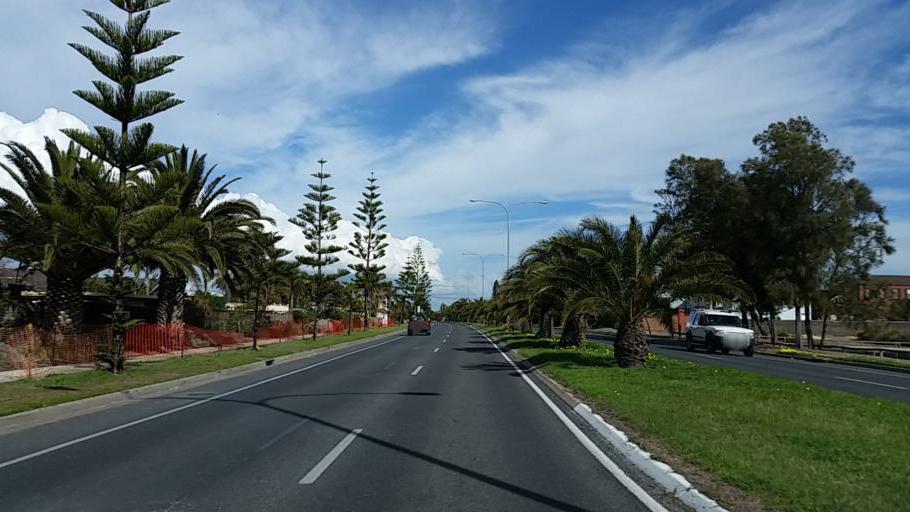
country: AU
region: South Australia
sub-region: Charles Sturt
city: West Lakes Shore
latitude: -34.8807
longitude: 138.4853
